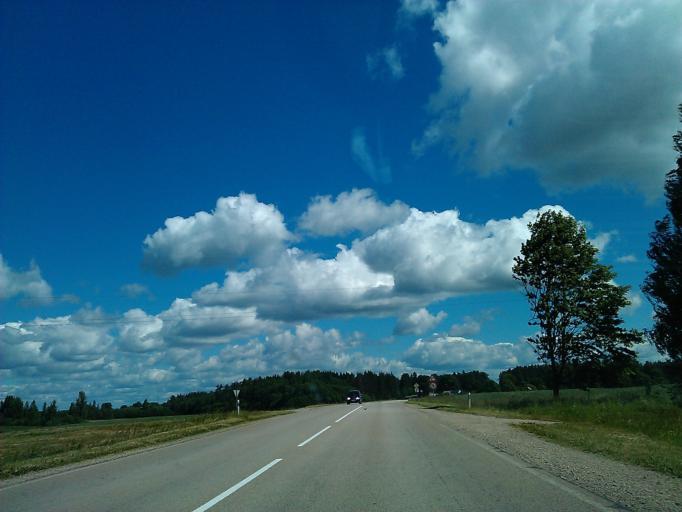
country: LV
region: Varaklani
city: Varaklani
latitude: 56.5969
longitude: 26.7267
